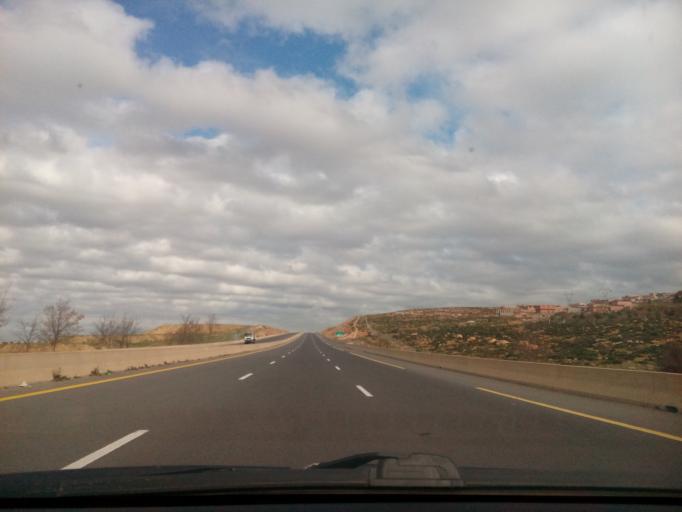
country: DZ
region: Tlemcen
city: Chetouane
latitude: 34.9528
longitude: -1.3011
